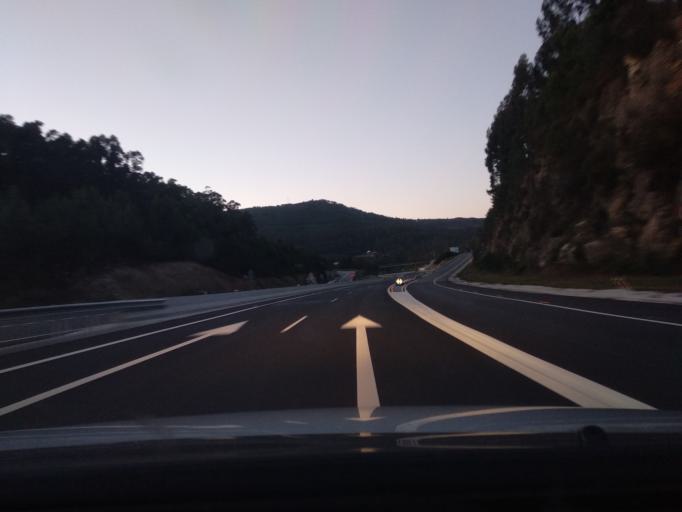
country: ES
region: Galicia
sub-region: Provincia de Pontevedra
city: Moana
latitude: 42.3018
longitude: -8.7193
